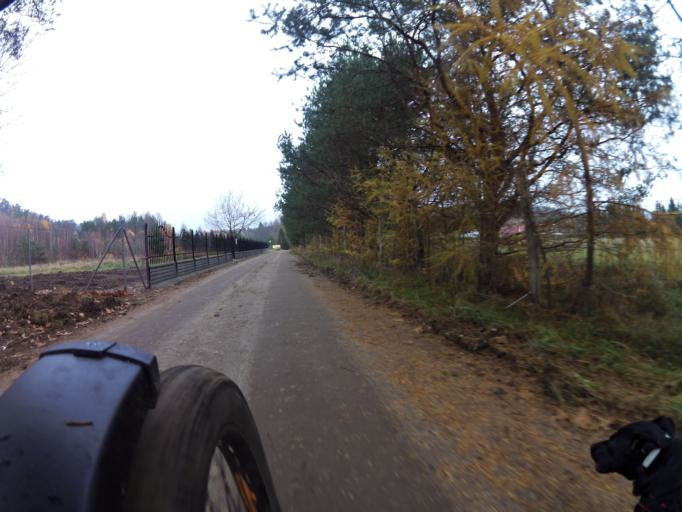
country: PL
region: Pomeranian Voivodeship
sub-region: Powiat wejherowski
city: Orle
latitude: 54.6890
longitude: 18.1512
